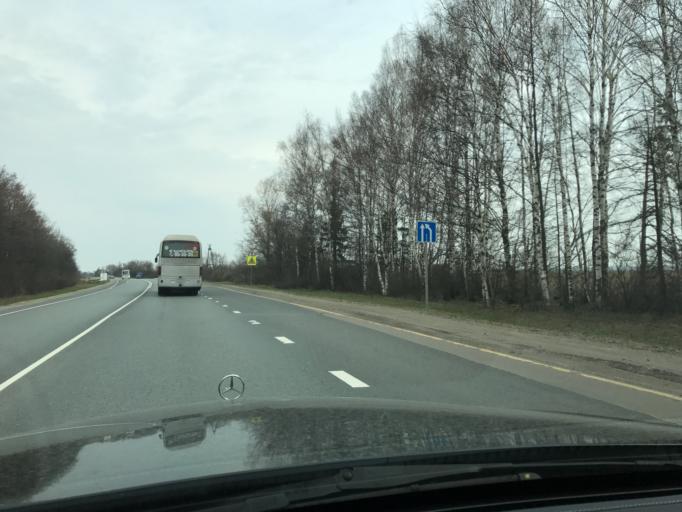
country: RU
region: Vladimir
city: Suzdal'
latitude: 56.3734
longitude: 40.4615
